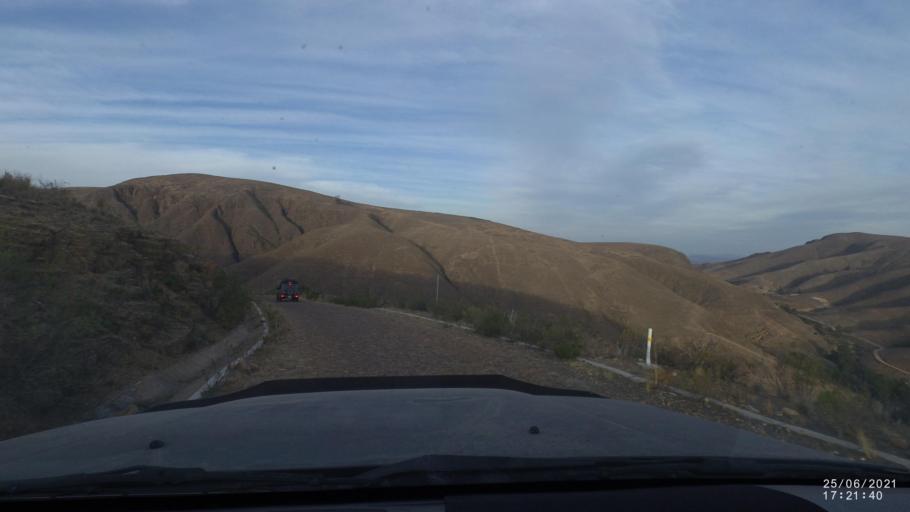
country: BO
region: Cochabamba
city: Mizque
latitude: -17.9098
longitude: -65.6867
